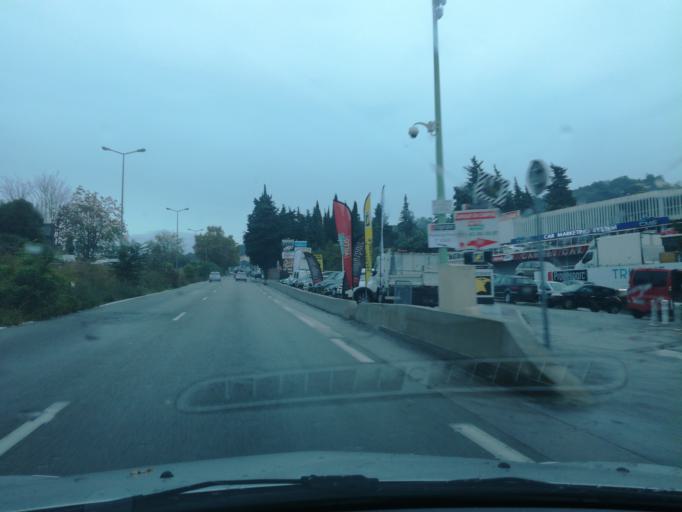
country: FR
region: Provence-Alpes-Cote d'Azur
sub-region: Departement des Alpes-Maritimes
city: Le Cannet
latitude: 43.5798
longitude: 7.0112
